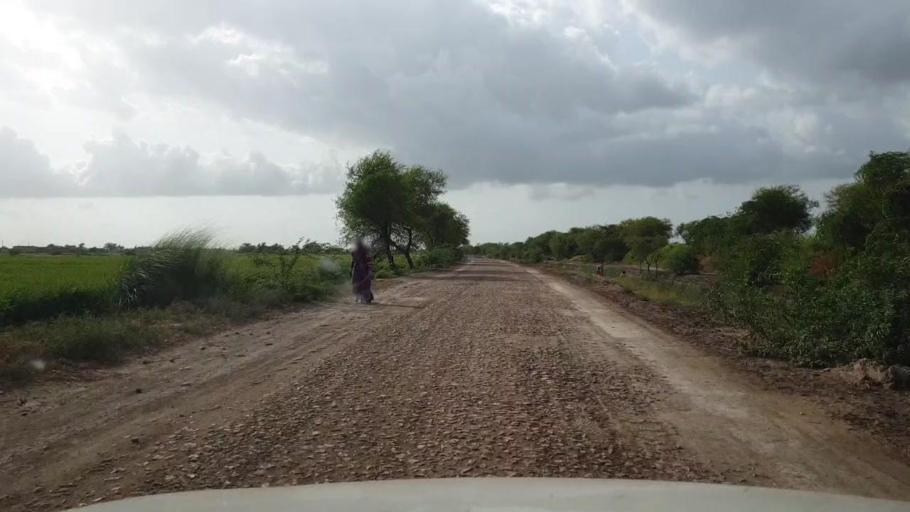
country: PK
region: Sindh
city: Kario
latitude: 24.7860
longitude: 68.5844
